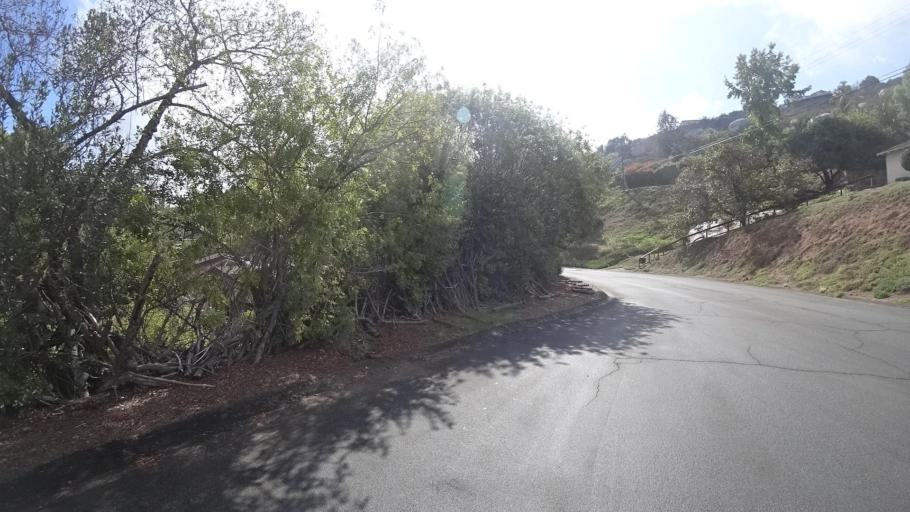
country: US
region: California
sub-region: San Diego County
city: Granite Hills
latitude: 32.7802
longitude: -116.9098
